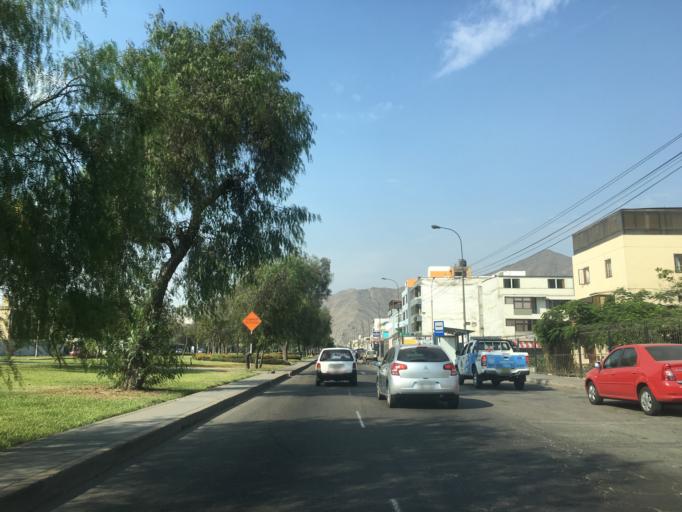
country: PE
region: Lima
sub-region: Lima
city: La Molina
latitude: -12.0682
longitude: -76.9464
